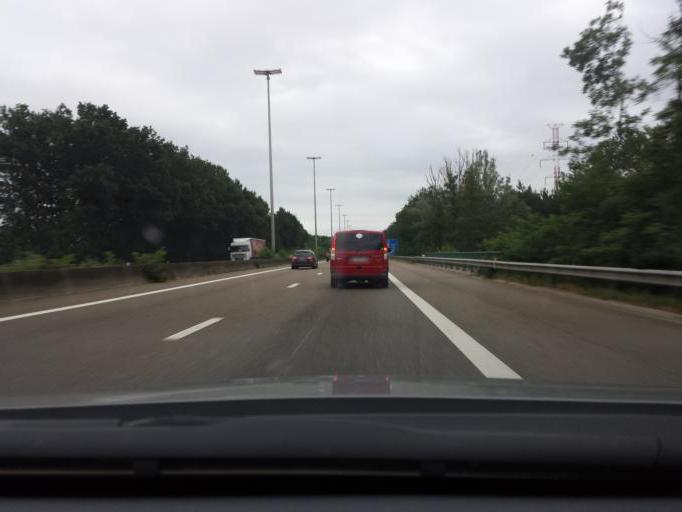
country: BE
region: Flanders
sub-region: Provincie Limburg
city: Lummen
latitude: 51.0165
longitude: 5.2104
